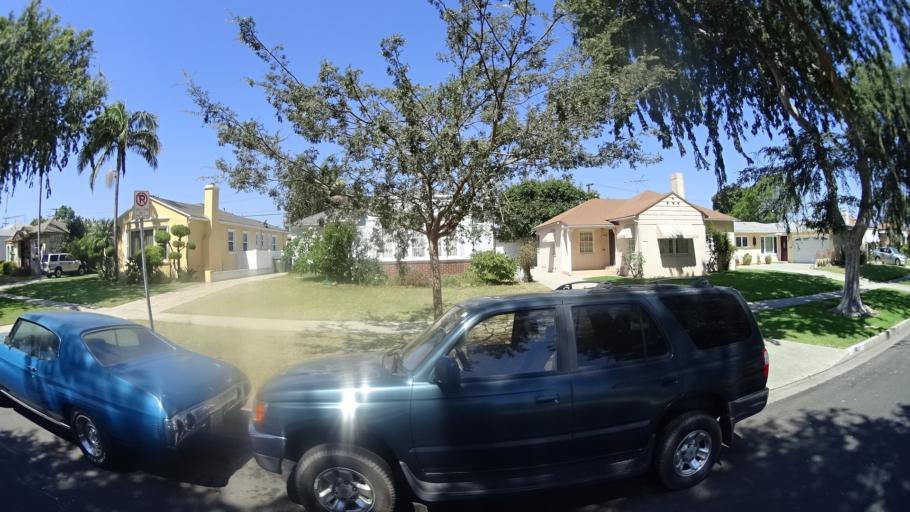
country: US
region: California
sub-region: Los Angeles County
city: View Park-Windsor Hills
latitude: 34.0242
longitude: -118.3593
